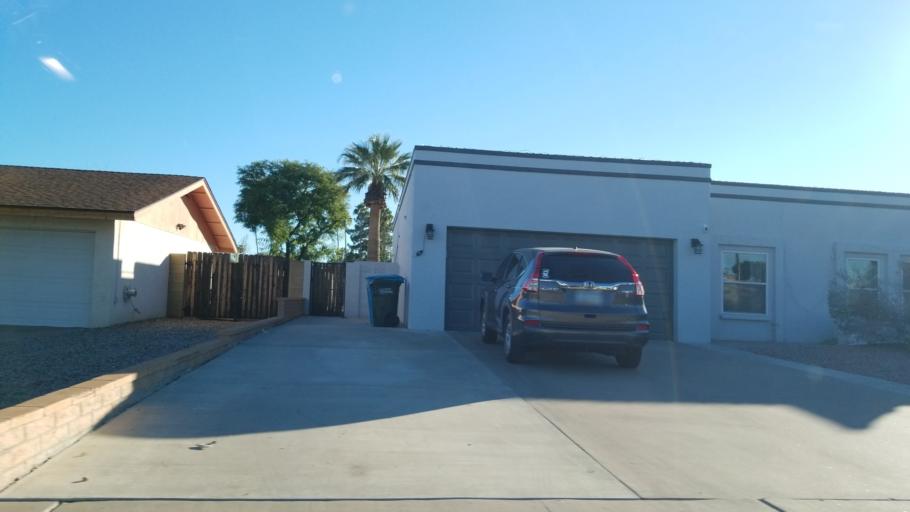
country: US
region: Arizona
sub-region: Maricopa County
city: Paradise Valley
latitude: 33.5994
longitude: -111.9715
